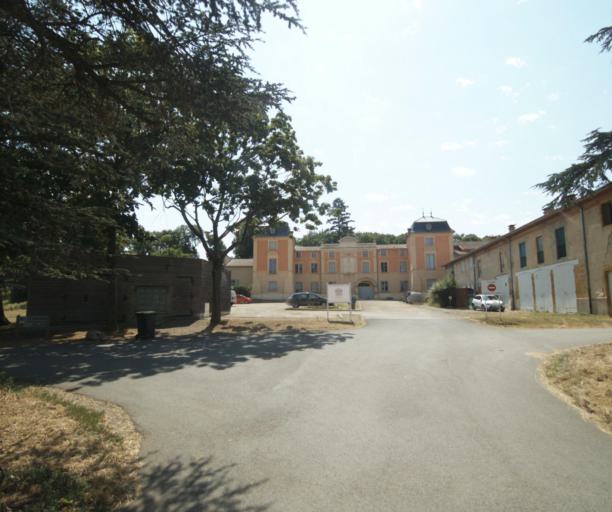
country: FR
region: Rhone-Alpes
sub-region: Departement du Rhone
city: Sourcieux-les-Mines
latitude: 45.8224
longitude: 4.6226
